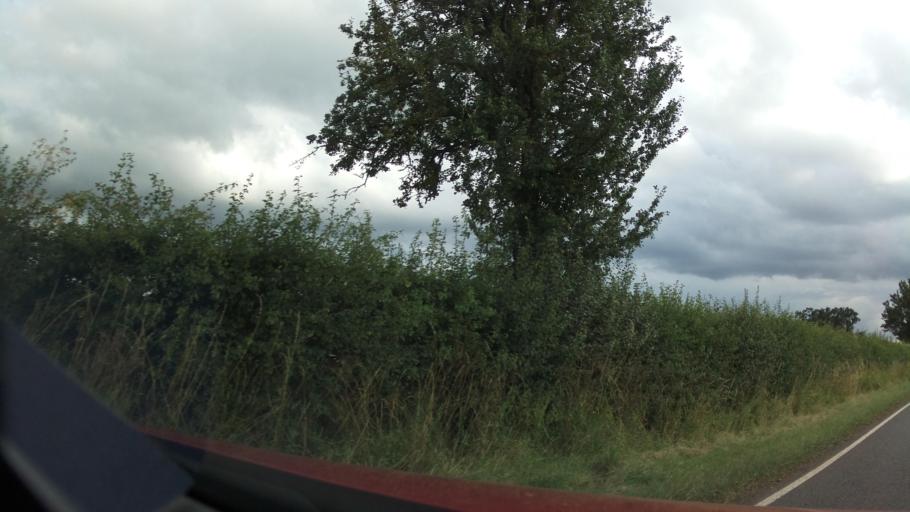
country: GB
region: England
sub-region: Warwickshire
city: Dunchurch
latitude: 52.3233
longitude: -1.3034
